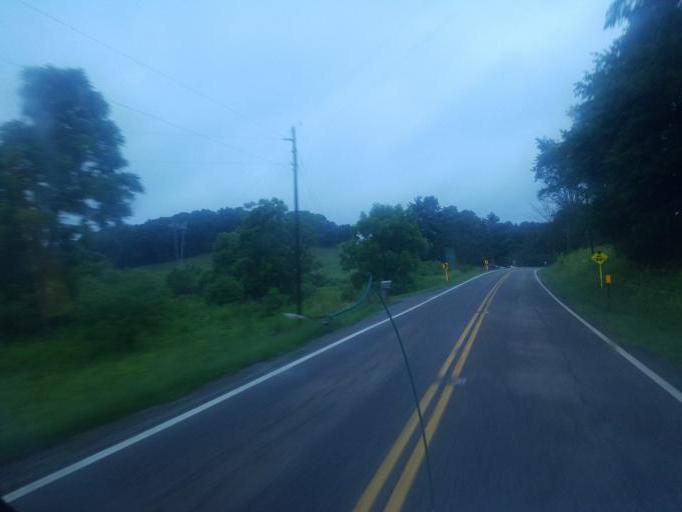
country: US
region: Ohio
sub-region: Carroll County
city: Carrollton
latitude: 40.5790
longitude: -81.0395
